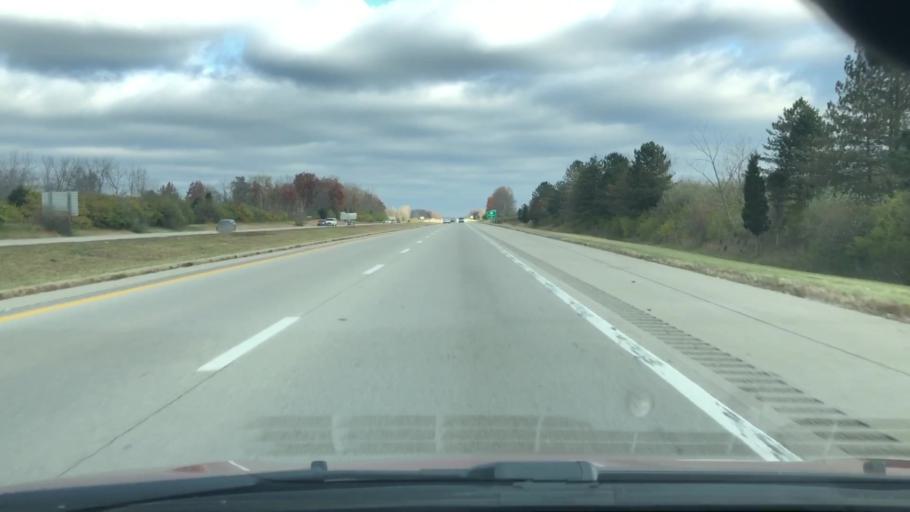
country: US
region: Ohio
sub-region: Greene County
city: Fairborn
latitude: 39.7926
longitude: -84.0025
